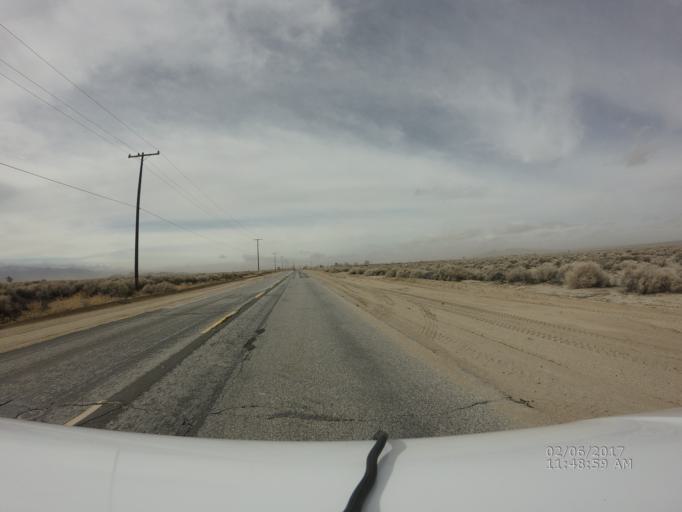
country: US
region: California
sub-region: Los Angeles County
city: Lake Los Angeles
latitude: 34.6019
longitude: -117.6936
